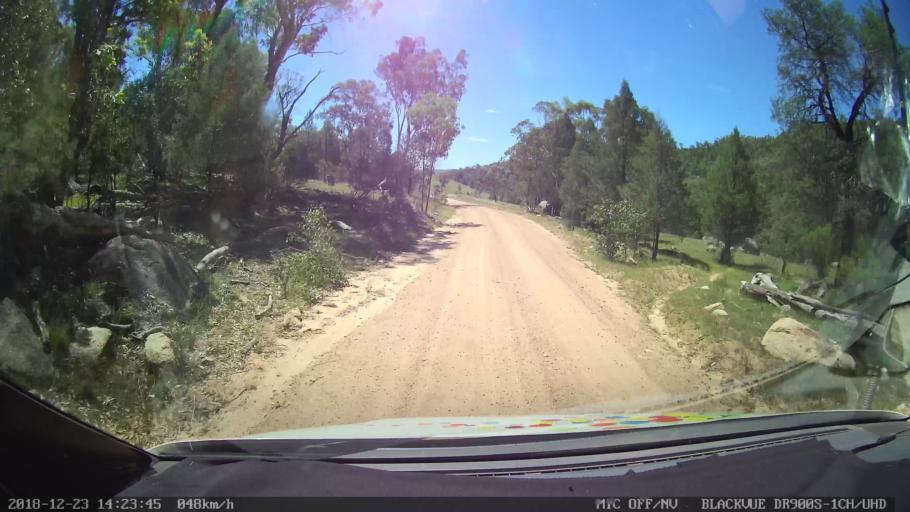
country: AU
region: New South Wales
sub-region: Tamworth Municipality
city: Manilla
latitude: -30.6351
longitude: 150.9654
